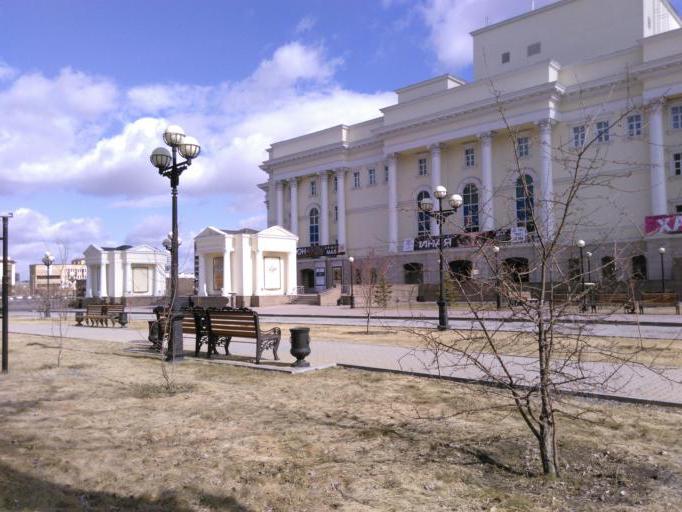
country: RU
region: Tjumen
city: Tyumen
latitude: 57.1436
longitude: 65.5594
